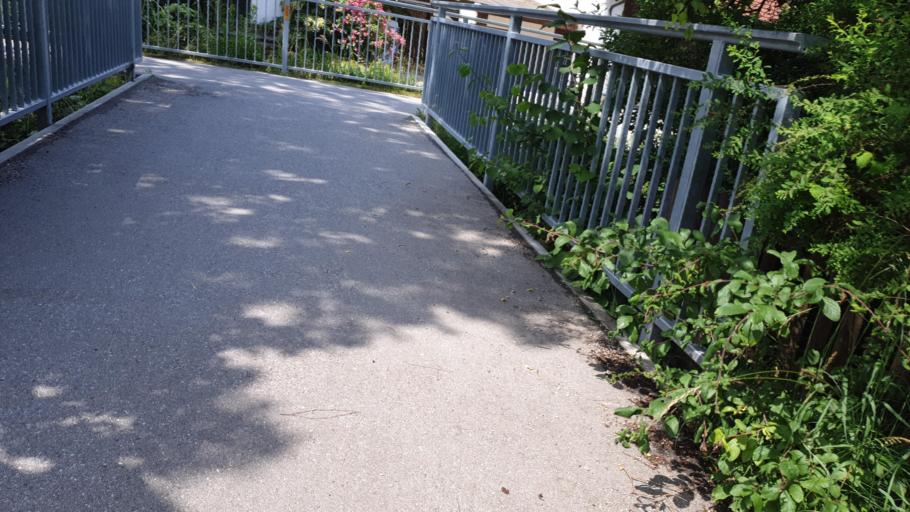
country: DE
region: Bavaria
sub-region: Upper Bavaria
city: Puchheim
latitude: 48.1492
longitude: 11.3487
